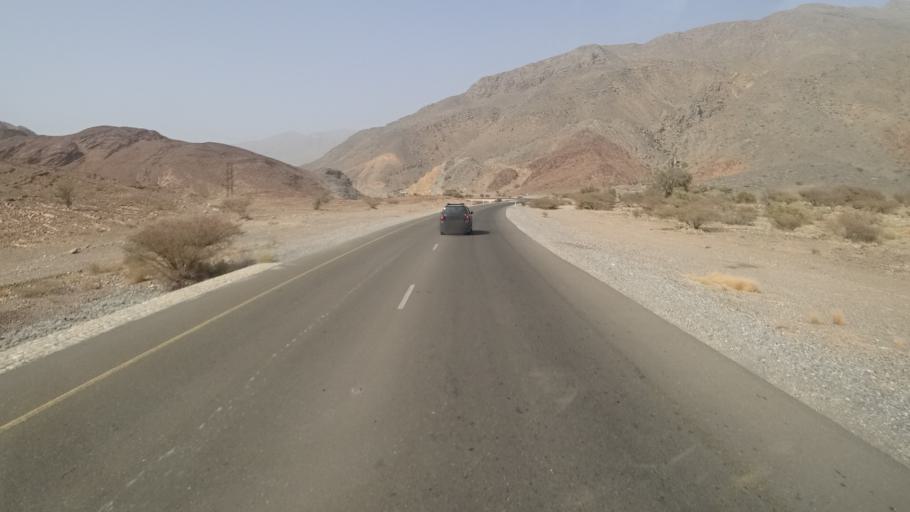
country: OM
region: Muhafazat ad Dakhiliyah
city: Nizwa
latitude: 22.9519
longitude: 57.5923
